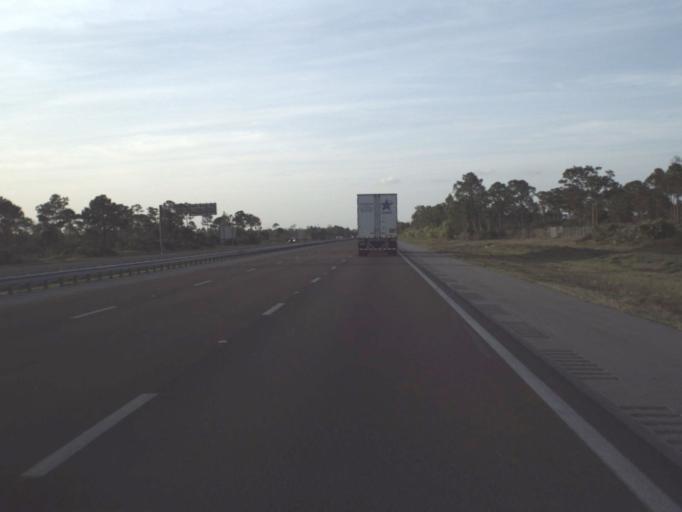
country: US
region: Florida
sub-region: Volusia County
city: Oak Hill
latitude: 28.7784
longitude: -80.8958
